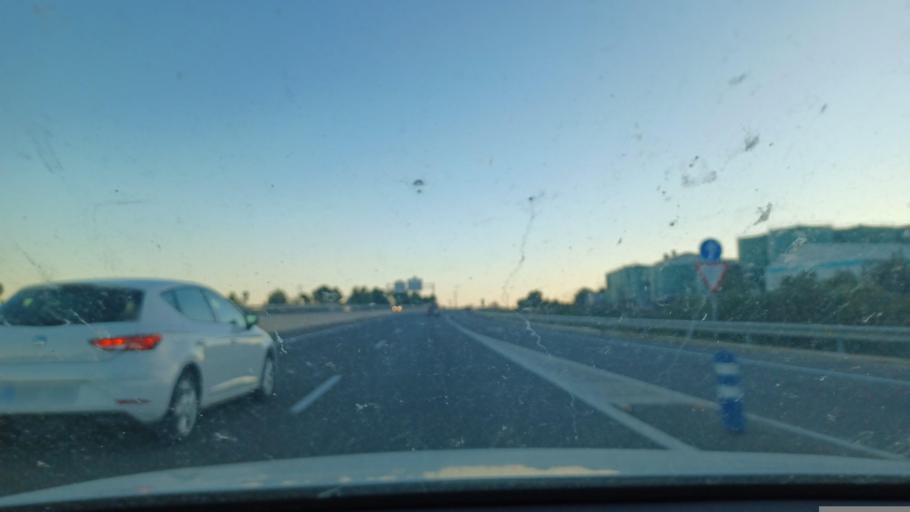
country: ES
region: Catalonia
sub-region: Provincia de Tarragona
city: Alcover
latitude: 41.2512
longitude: 1.1730
